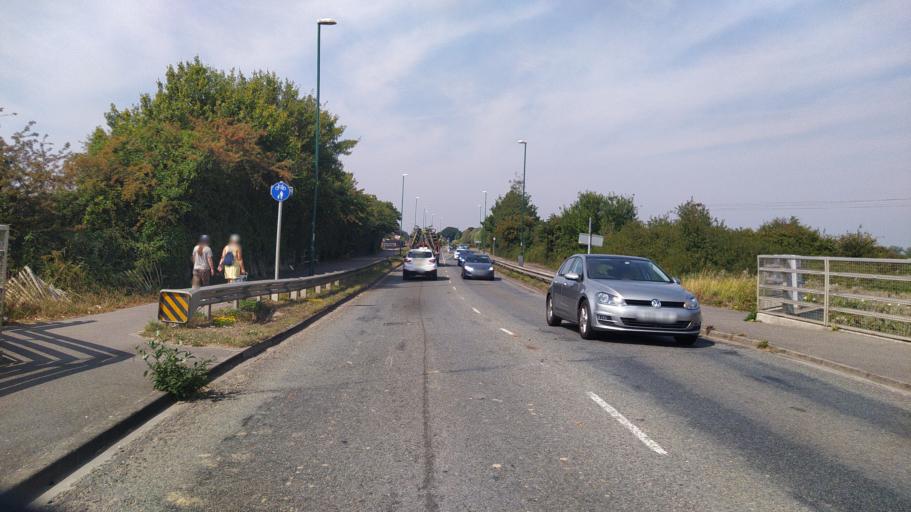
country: GB
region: England
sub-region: West Sussex
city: Bognor Regis
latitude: 50.8032
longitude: -0.6731
